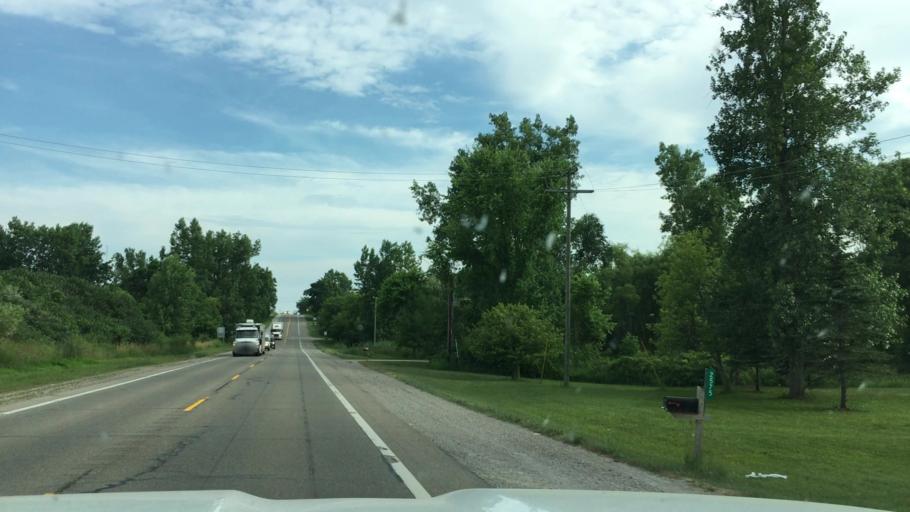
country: US
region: Michigan
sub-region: Lapeer County
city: Imlay City
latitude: 43.1114
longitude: -83.0725
